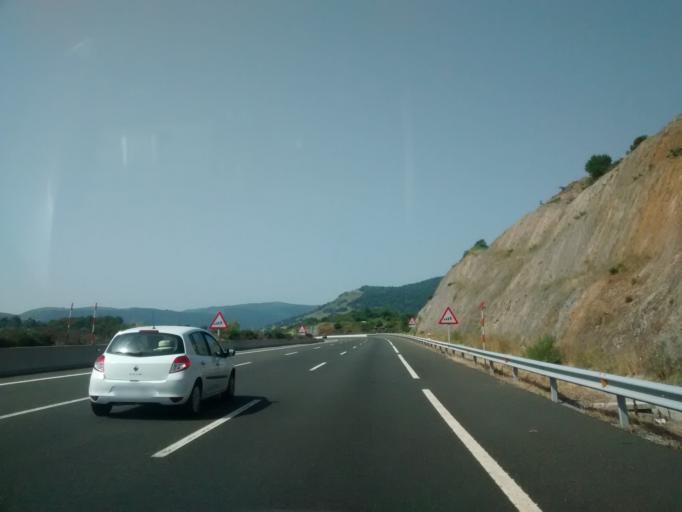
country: ES
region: Cantabria
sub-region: Provincia de Cantabria
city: Barcena de Pie de Concha
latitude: 43.1315
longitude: -4.0701
